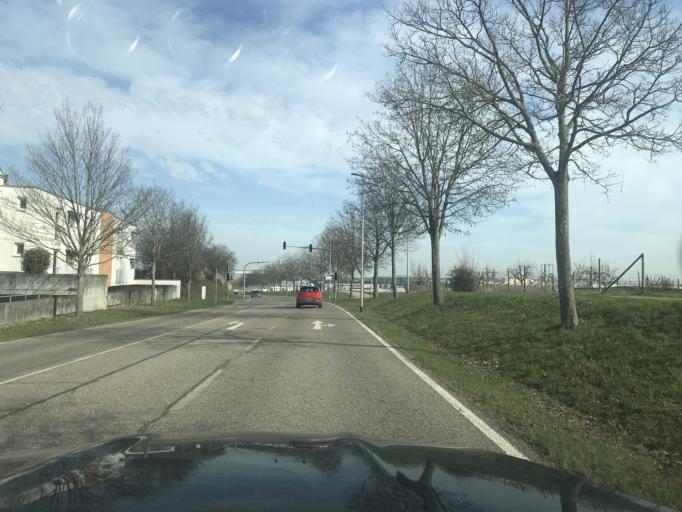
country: DE
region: Baden-Wuerttemberg
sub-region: Regierungsbezirk Stuttgart
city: Fellbach
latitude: 48.8078
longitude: 9.2878
